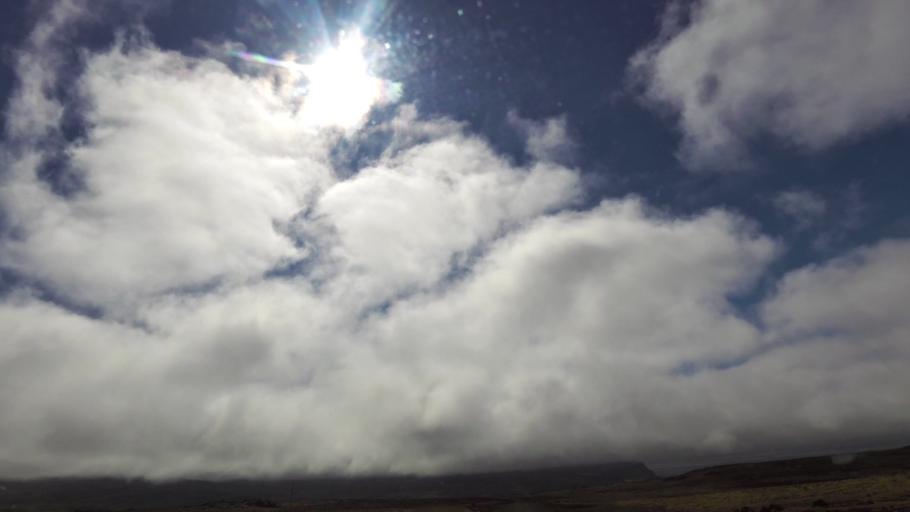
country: IS
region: West
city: Olafsvik
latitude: 65.5517
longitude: -24.2655
